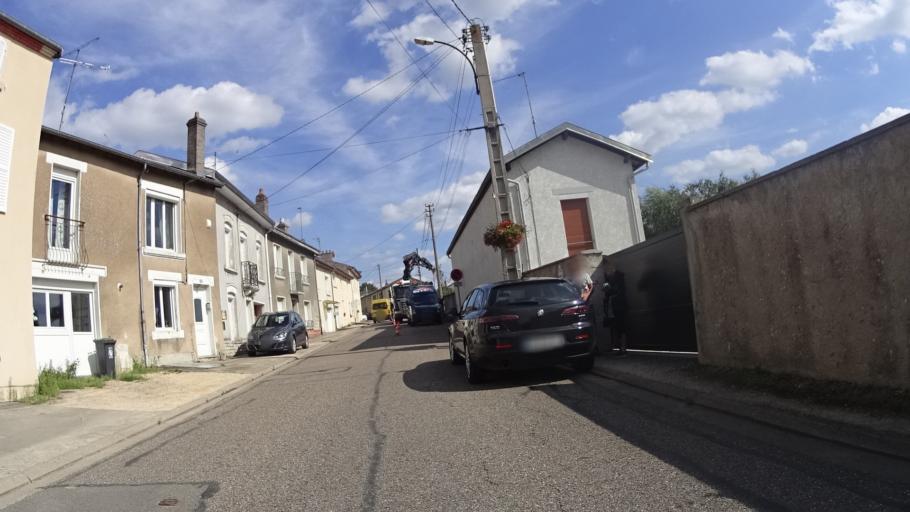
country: FR
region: Lorraine
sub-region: Departement de Meurthe-et-Moselle
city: Dommartin-les-Toul
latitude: 48.6540
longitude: 5.9041
